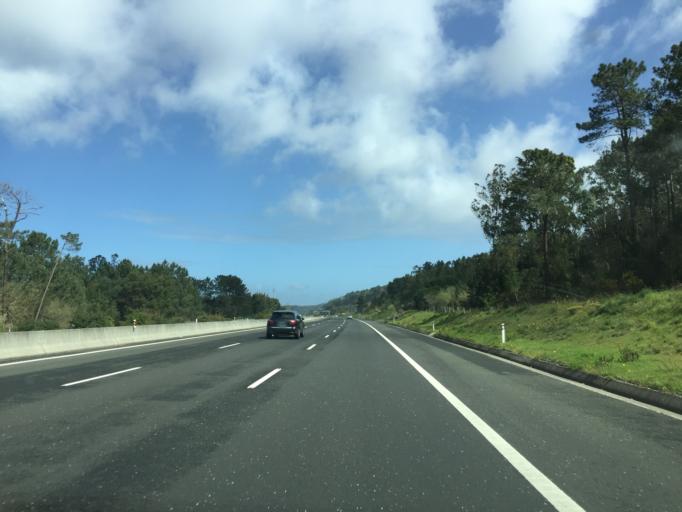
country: PT
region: Leiria
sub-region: Caldas da Rainha
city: Caldas da Rainha
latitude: 39.4755
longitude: -9.1038
